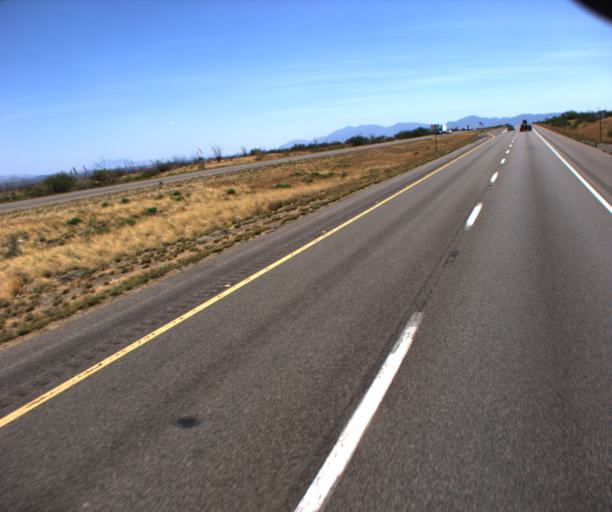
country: US
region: Arizona
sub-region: Cochise County
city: Whetstone
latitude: 31.8298
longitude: -110.3449
